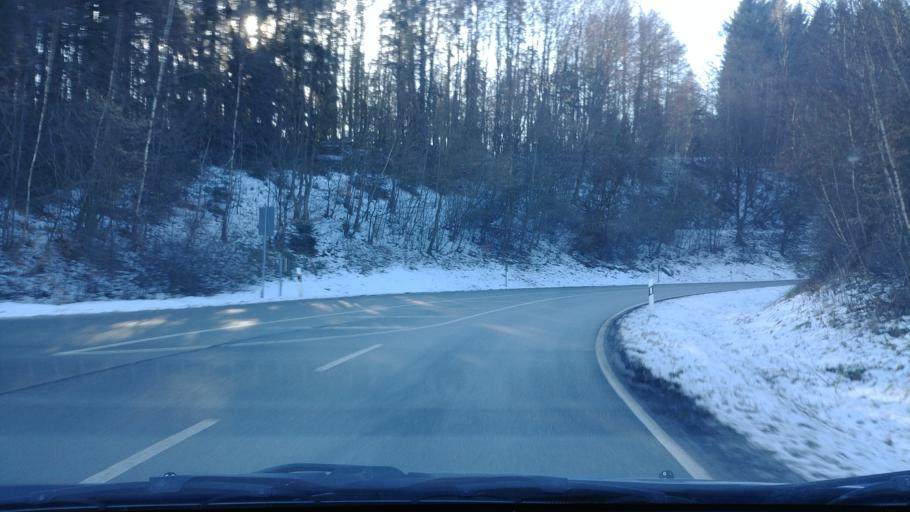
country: DE
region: Hesse
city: Trendelburg
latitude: 51.5707
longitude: 9.4798
